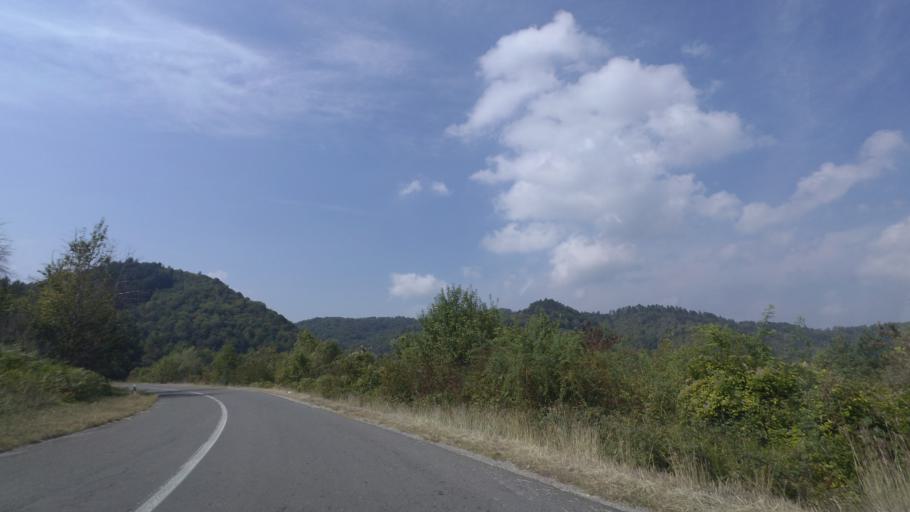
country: BA
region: Federation of Bosnia and Herzegovina
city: Zboriste
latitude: 45.1656
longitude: 16.1386
